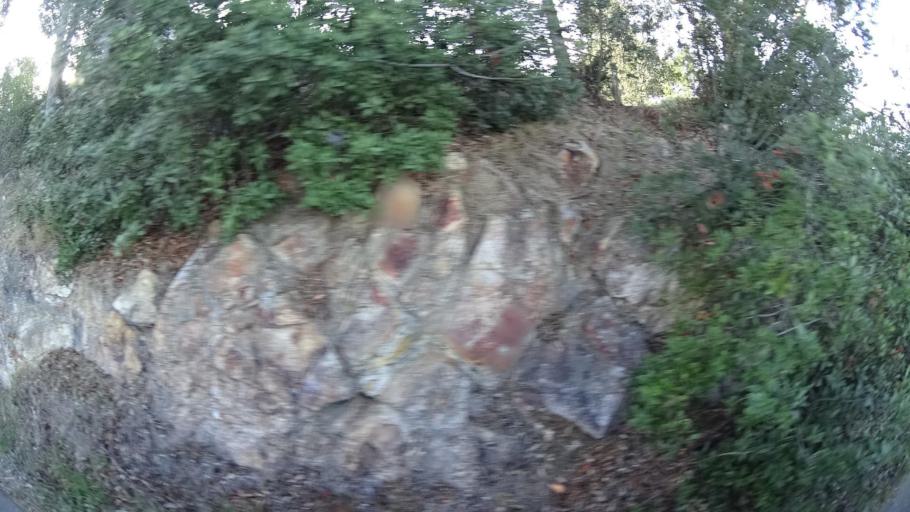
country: US
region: California
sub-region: San Diego County
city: Spring Valley
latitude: 32.7352
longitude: -116.9876
